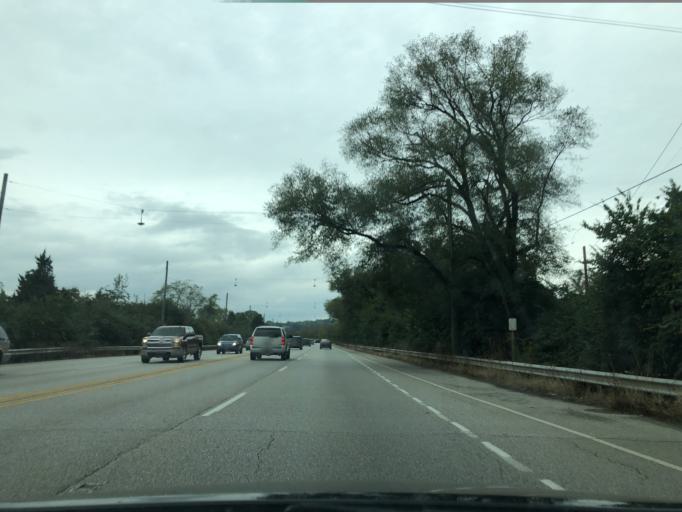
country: US
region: Ohio
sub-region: Hamilton County
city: Turpin Hills
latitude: 39.1101
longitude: -84.4023
